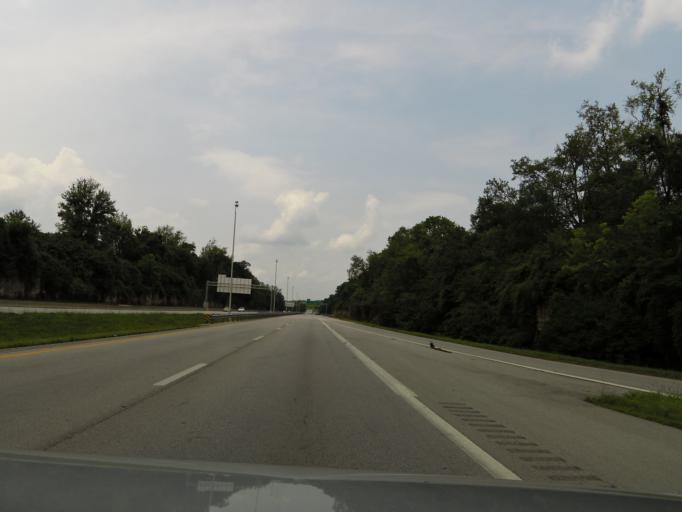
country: US
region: Kentucky
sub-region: Jefferson County
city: Northfield
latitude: 38.2818
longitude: -85.6383
